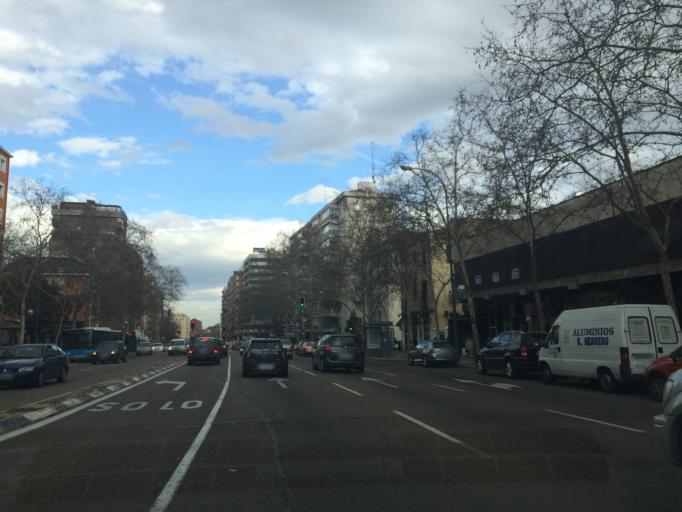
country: ES
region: Madrid
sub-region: Provincia de Madrid
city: Chamartin
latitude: 40.4586
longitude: -3.6833
